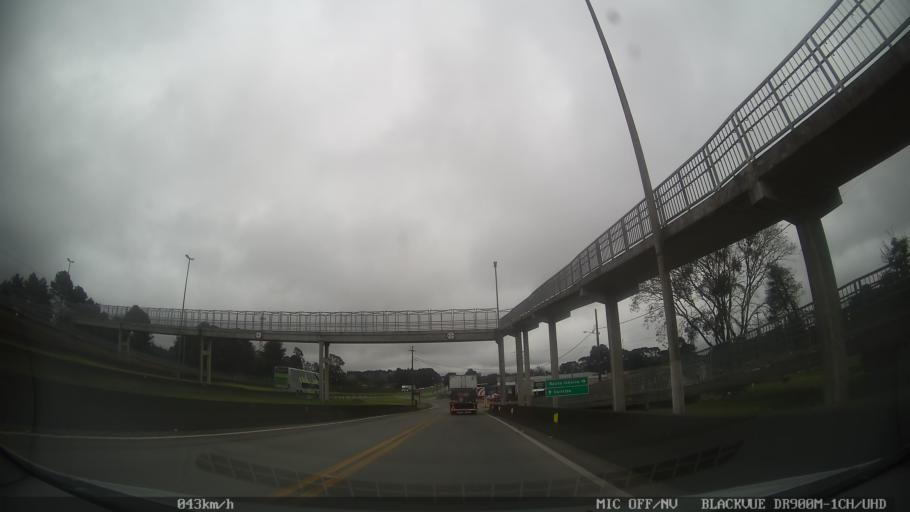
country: BR
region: Parana
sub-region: Sao Jose Dos Pinhais
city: Sao Jose dos Pinhais
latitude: -25.6645
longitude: -49.1535
